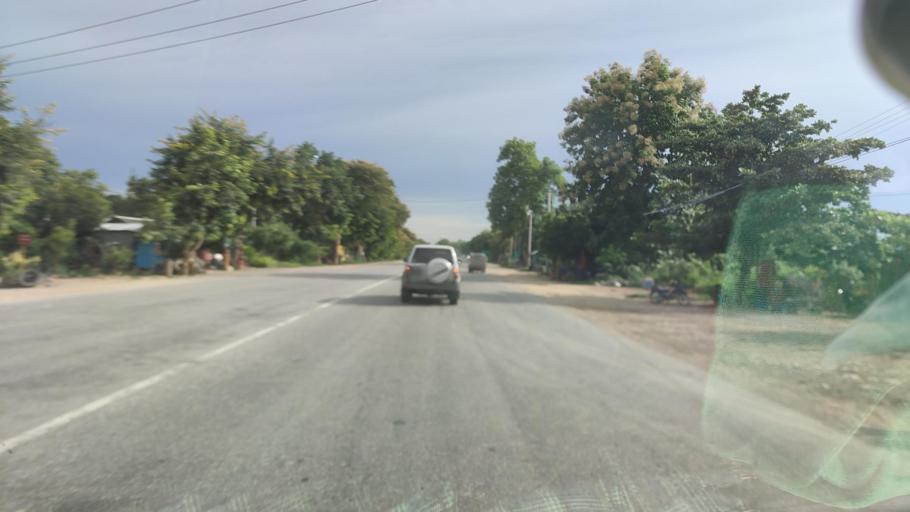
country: MM
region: Mandalay
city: Kyaukse
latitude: 21.4998
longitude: 96.1829
